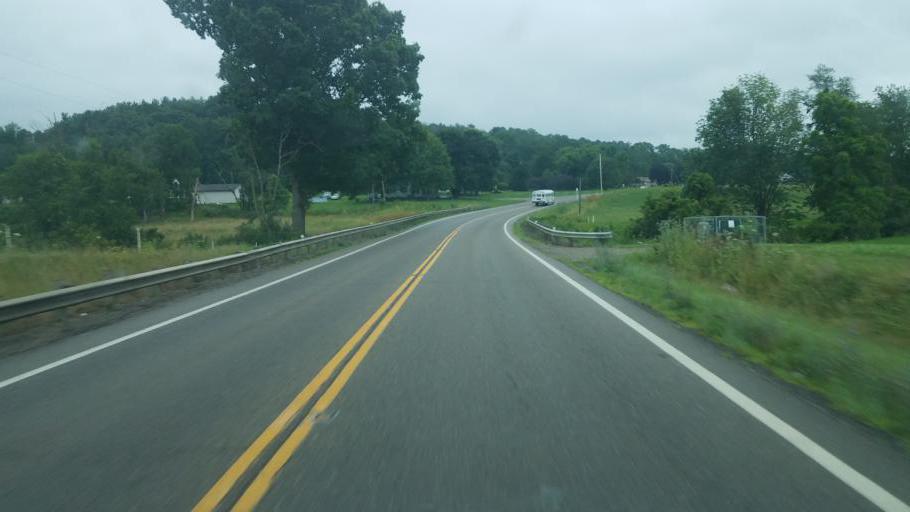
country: US
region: Ohio
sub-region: Tuscarawas County
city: Dennison
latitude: 40.4077
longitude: -81.2822
